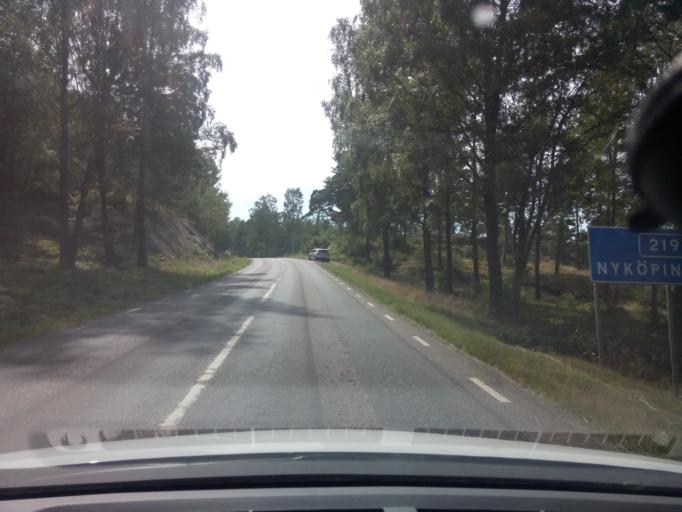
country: SE
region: Soedermanland
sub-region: Oxelosunds Kommun
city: Oxelosund
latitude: 58.7625
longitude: 17.3301
